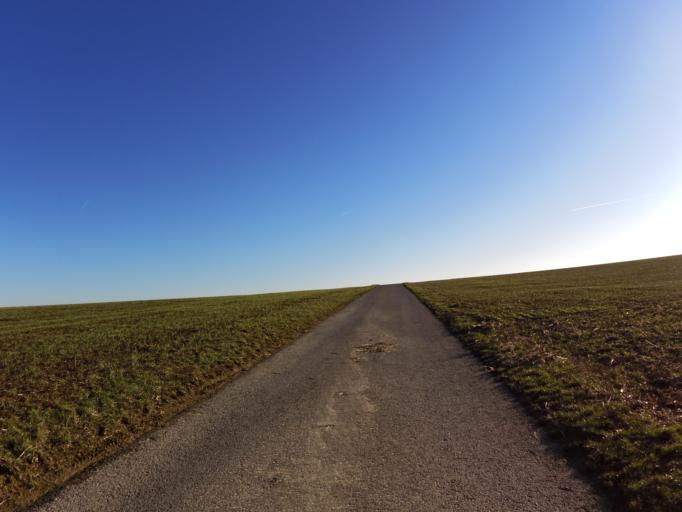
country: DE
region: Bavaria
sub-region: Regierungsbezirk Unterfranken
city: Estenfeld
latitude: 49.8489
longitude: 9.9981
